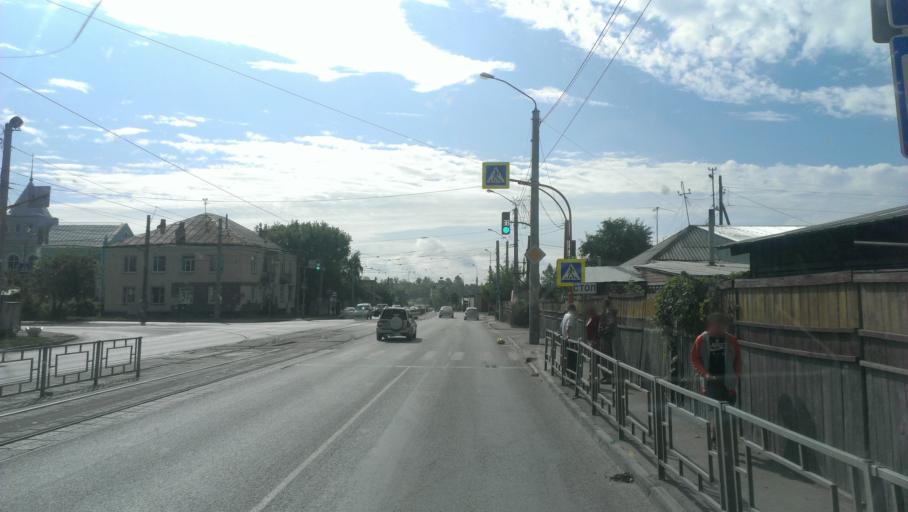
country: RU
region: Altai Krai
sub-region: Gorod Barnaulskiy
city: Barnaul
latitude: 53.3448
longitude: 83.7338
